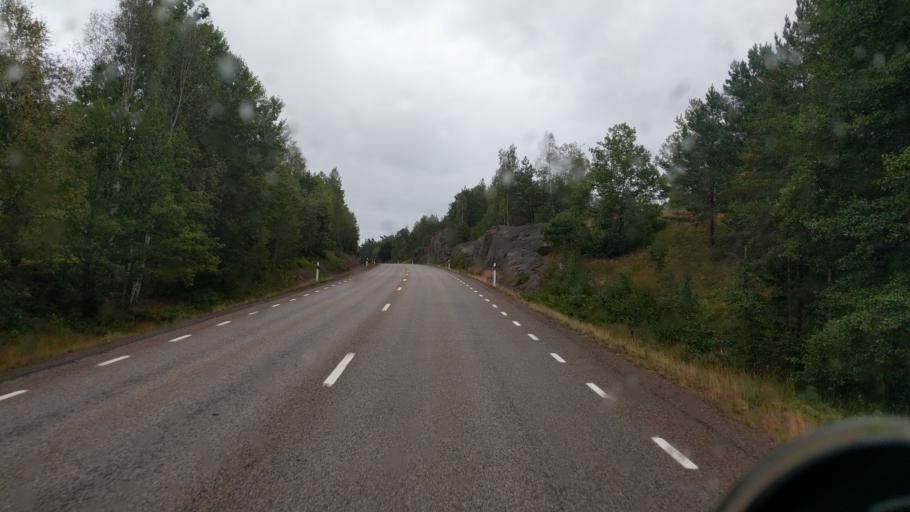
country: SE
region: Kalmar
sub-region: Vasterviks Kommun
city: Ankarsrum
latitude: 57.7031
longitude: 16.3188
